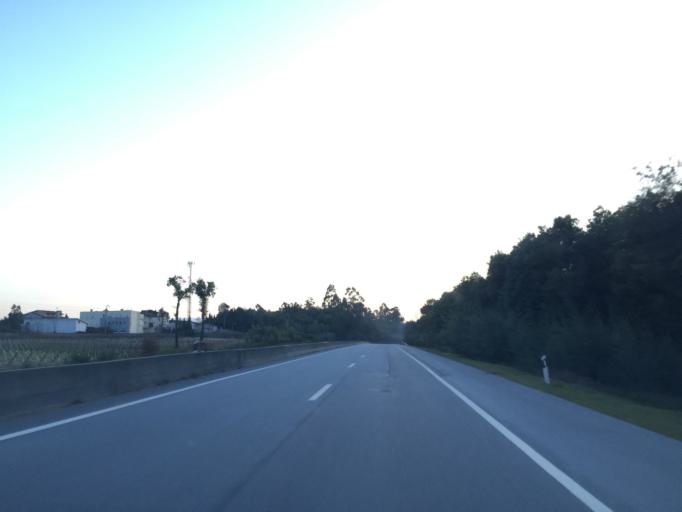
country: PT
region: Viseu
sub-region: Concelho de Carregal do Sal
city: Carregal do Sal
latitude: 40.4427
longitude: -7.9864
